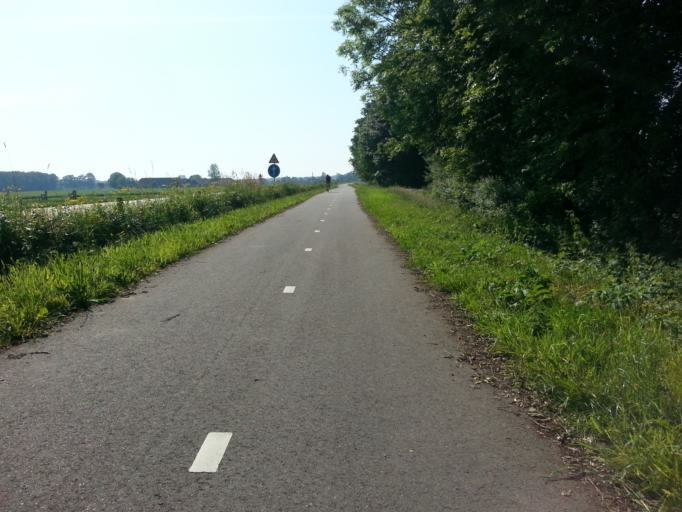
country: NL
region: Utrecht
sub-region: Gemeente Utrechtse Heuvelrug
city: Driebergen-Rijsenburg
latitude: 52.0264
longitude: 5.2503
